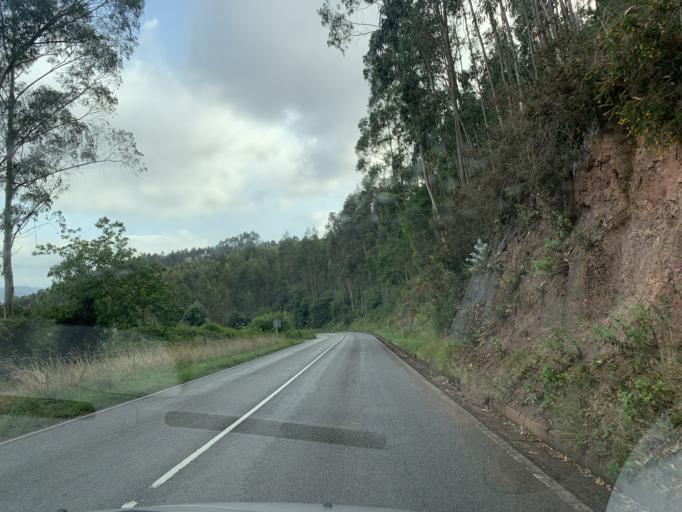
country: ES
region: Asturias
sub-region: Province of Asturias
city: Villaviciosa
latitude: 43.5153
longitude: -5.4268
